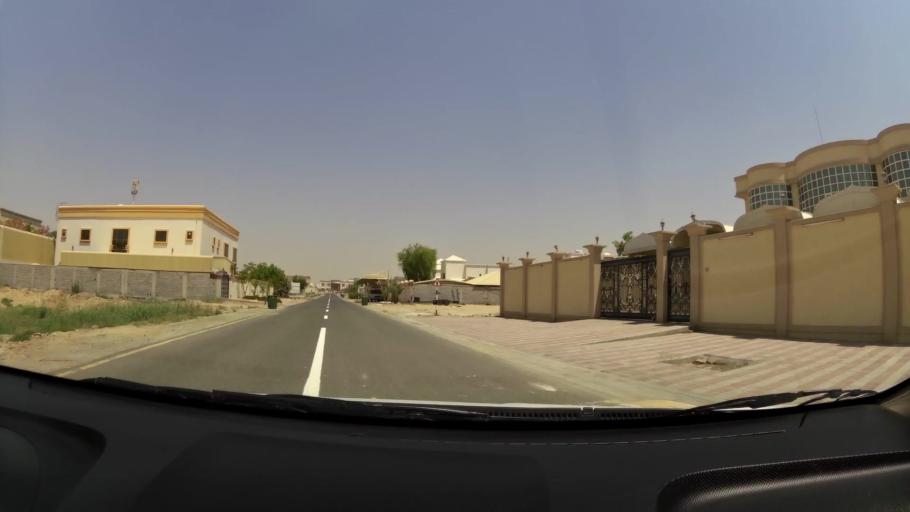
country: AE
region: Ajman
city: Ajman
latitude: 25.4226
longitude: 55.5121
